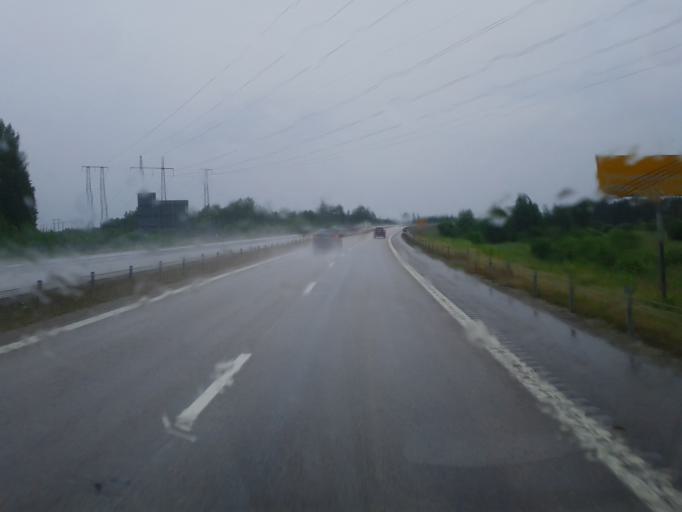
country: SE
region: Uppsala
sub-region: Tierps Kommun
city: Tierp
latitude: 60.3547
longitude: 17.4731
